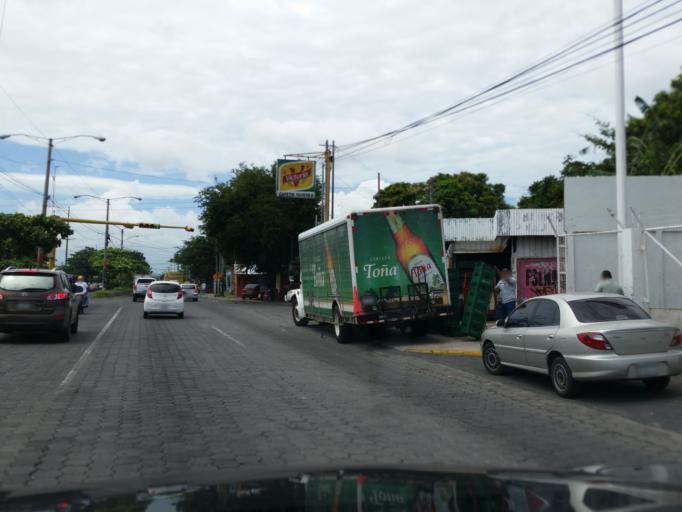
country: NI
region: Managua
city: Managua
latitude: 12.1286
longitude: -86.2337
